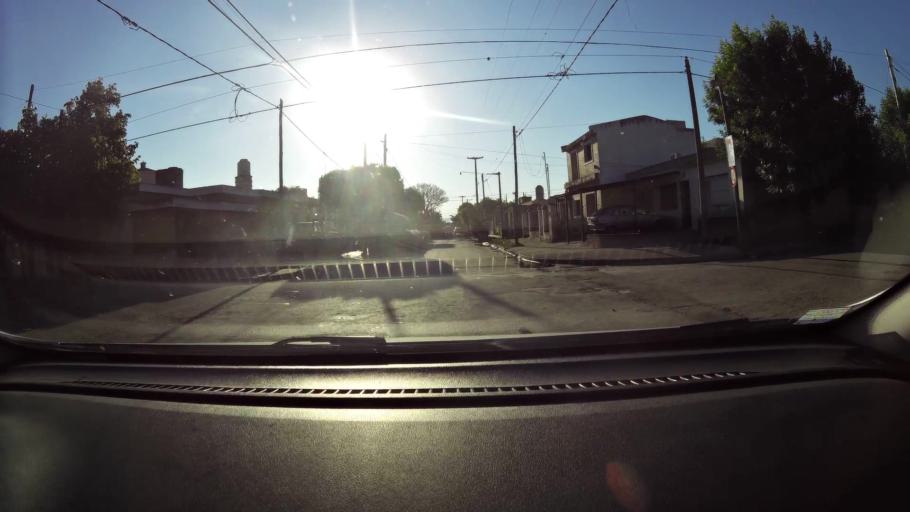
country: AR
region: Cordoba
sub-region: Departamento de Capital
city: Cordoba
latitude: -31.3752
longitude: -64.1935
